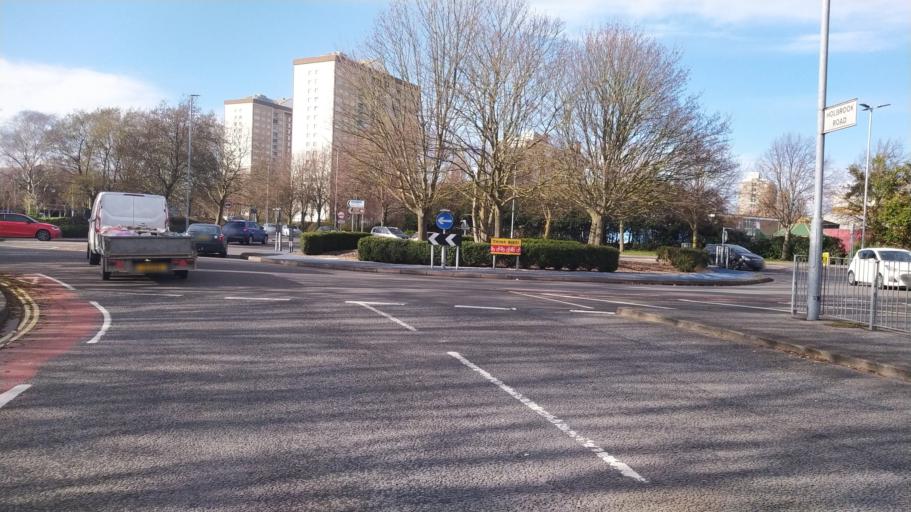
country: GB
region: England
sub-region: Portsmouth
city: Portsmouth
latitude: 50.8036
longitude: -1.0828
